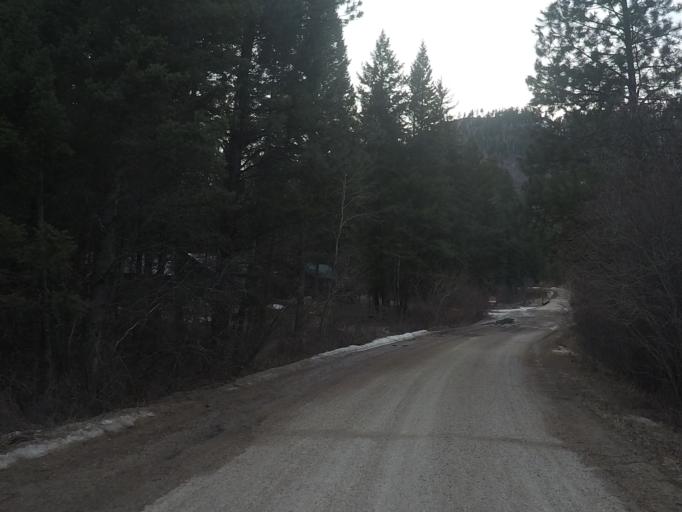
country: US
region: Montana
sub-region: Ravalli County
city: Hamilton
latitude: 45.8440
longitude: -114.0369
